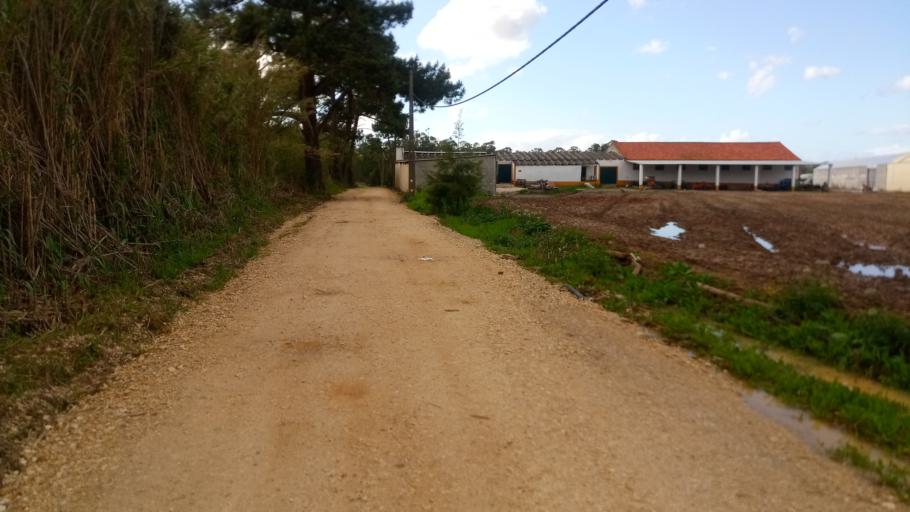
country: PT
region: Leiria
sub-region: Caldas da Rainha
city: Caldas da Rainha
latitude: 39.4341
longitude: -9.1636
